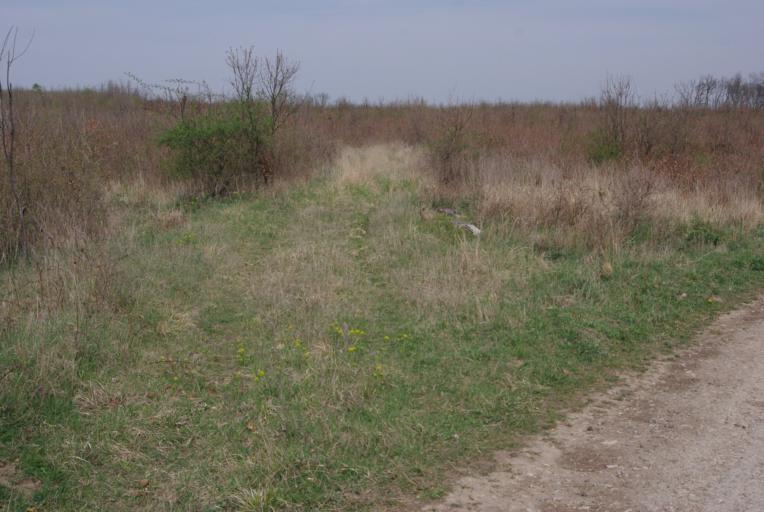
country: HU
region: Fejer
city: Csakvar
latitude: 47.4373
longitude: 18.4631
